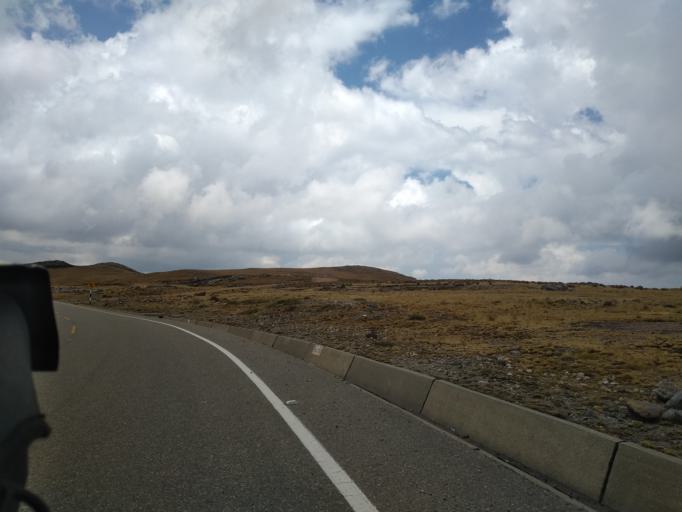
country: PE
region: La Libertad
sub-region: Provincia de Santiago de Chuco
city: Quiruvilca
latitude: -7.9676
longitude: -78.2028
